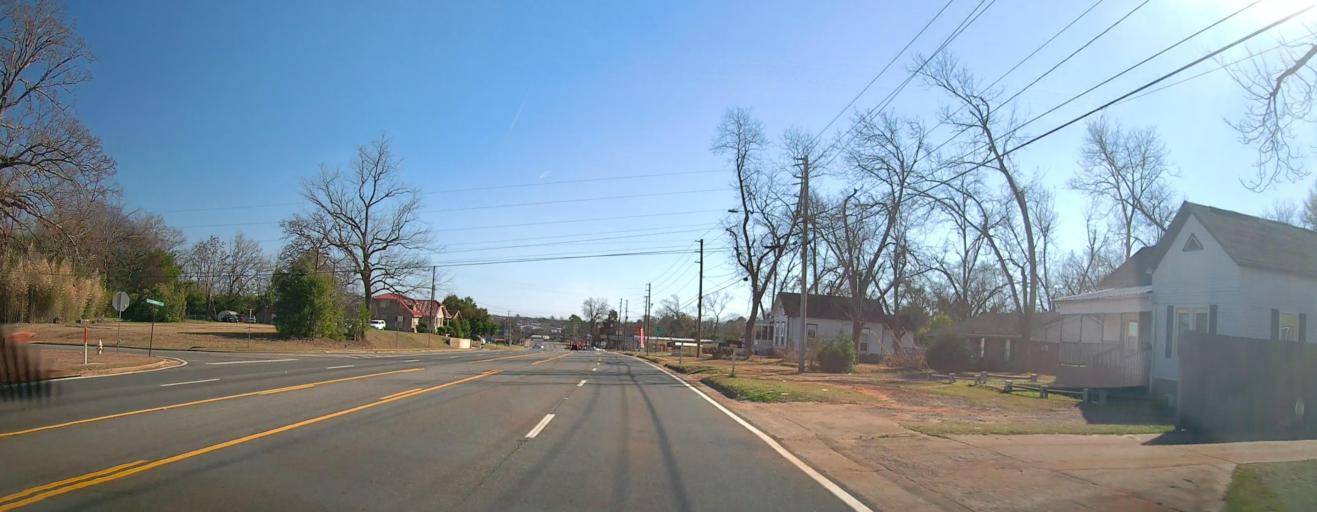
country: US
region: Georgia
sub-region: Sumter County
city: Americus
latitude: 32.0876
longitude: -84.2404
